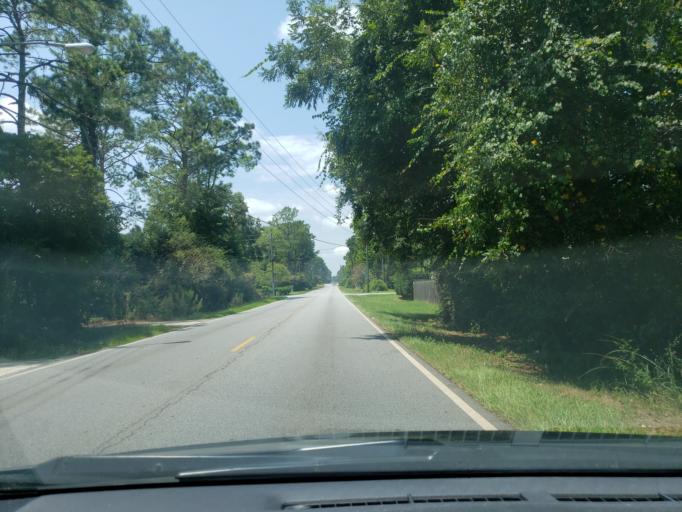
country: US
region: Georgia
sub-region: Dougherty County
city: Albany
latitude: 31.6135
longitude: -84.2309
